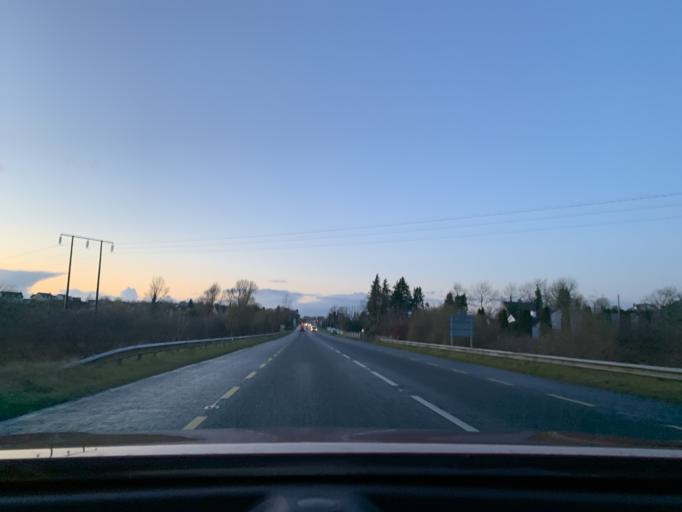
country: IE
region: Connaught
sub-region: County Leitrim
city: Carrick-on-Shannon
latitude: 53.9407
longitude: -8.0644
